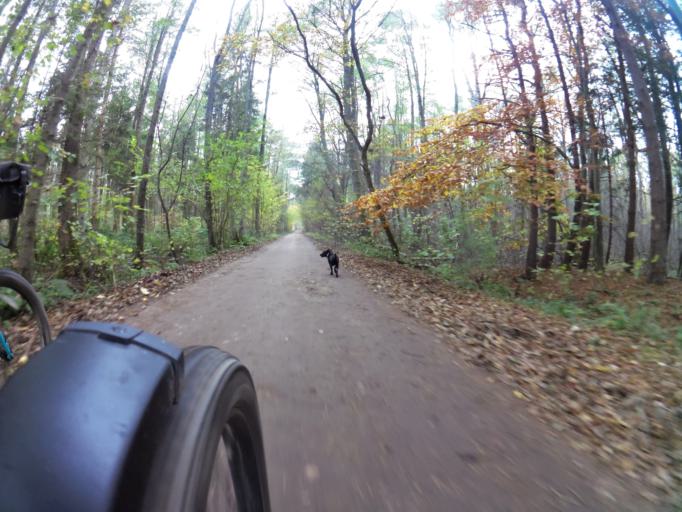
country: PL
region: Pomeranian Voivodeship
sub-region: Powiat pucki
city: Krokowa
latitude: 54.8292
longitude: 18.1110
